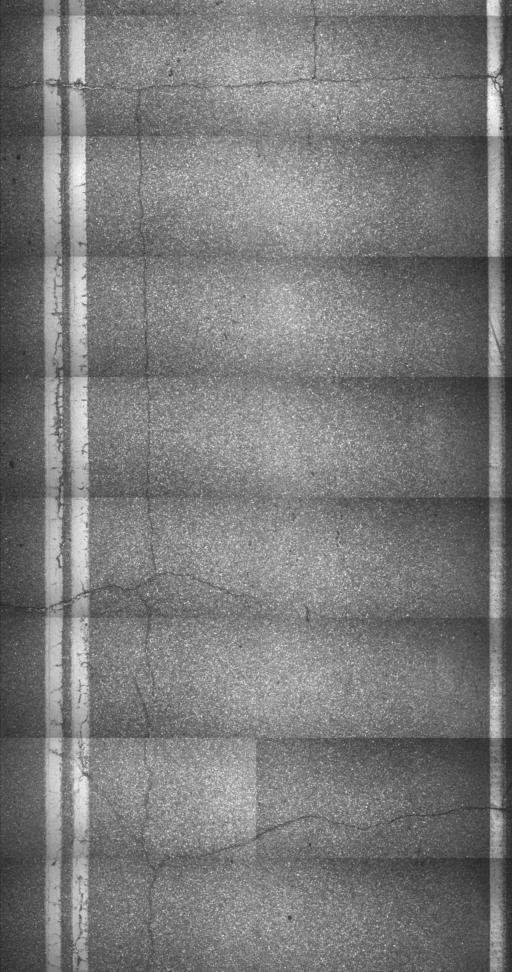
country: US
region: Vermont
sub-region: Windsor County
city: Windsor
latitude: 43.4575
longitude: -72.3943
